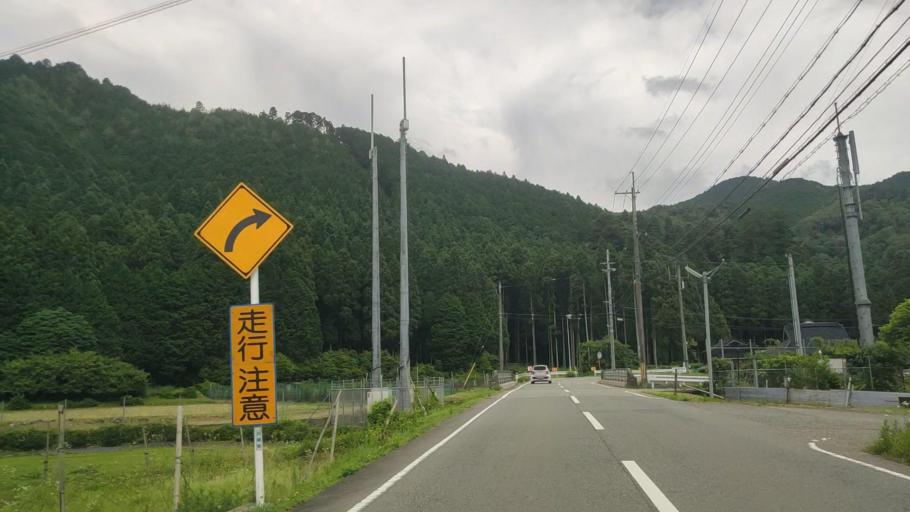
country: JP
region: Hyogo
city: Nishiwaki
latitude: 35.1873
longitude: 134.9297
